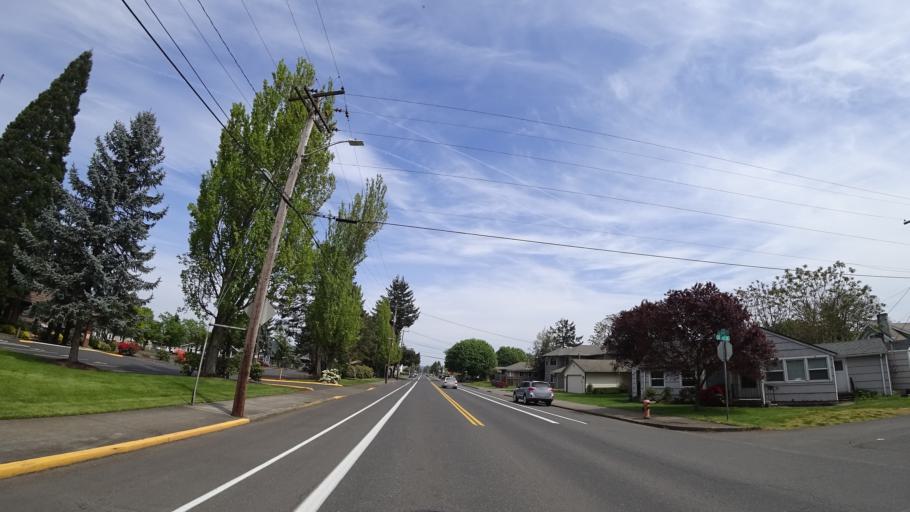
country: US
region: Oregon
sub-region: Multnomah County
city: Lents
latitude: 45.4759
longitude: -122.6060
